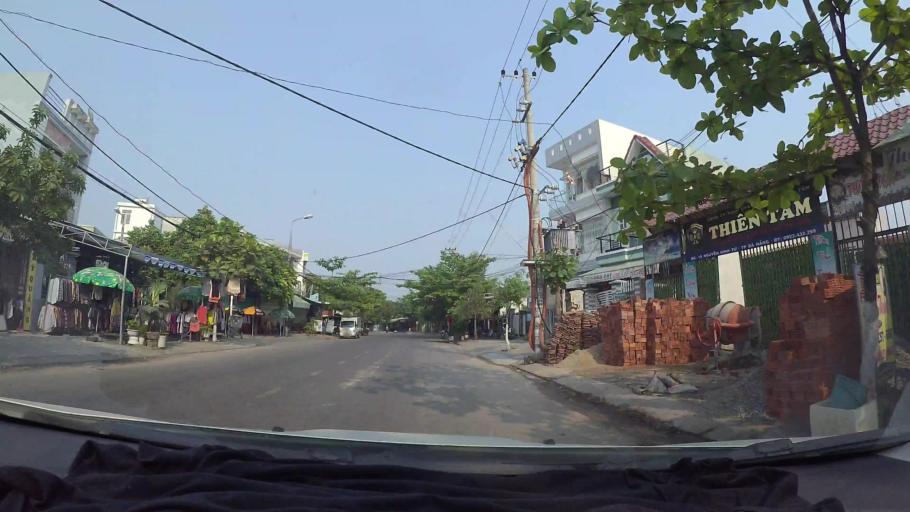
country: VN
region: Da Nang
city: Lien Chieu
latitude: 16.0488
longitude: 108.1724
